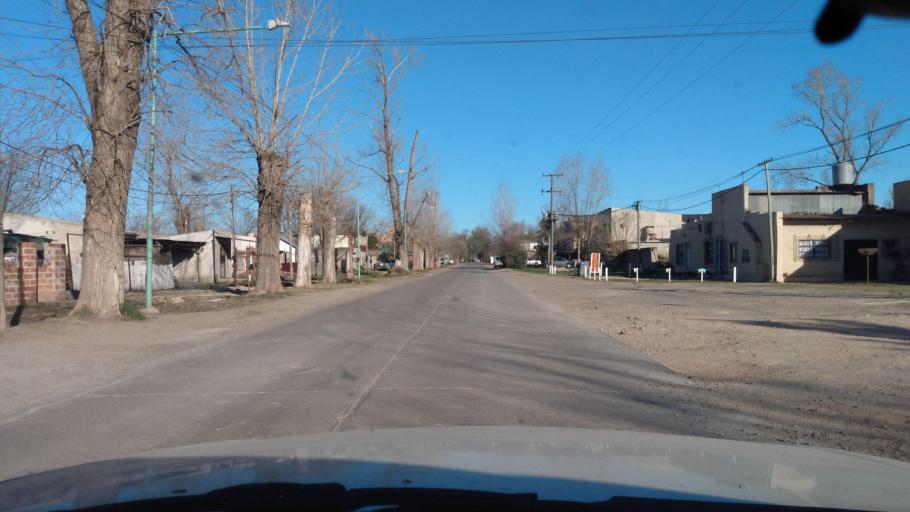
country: AR
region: Buenos Aires
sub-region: Partido de Lujan
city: Lujan
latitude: -34.6228
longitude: -59.2557
